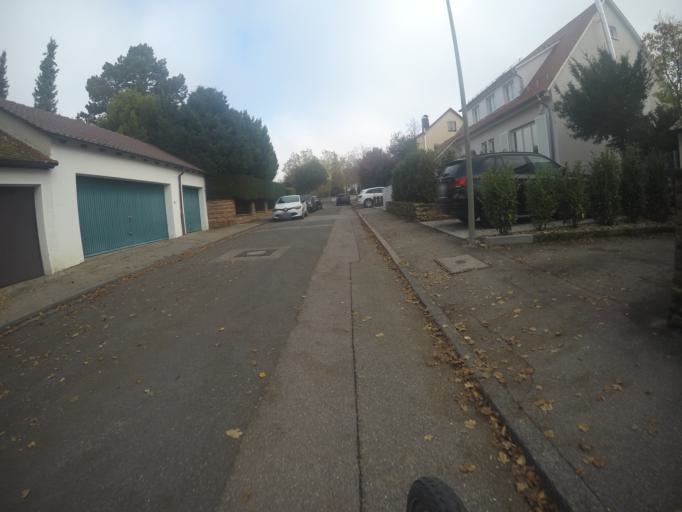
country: DE
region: Baden-Wuerttemberg
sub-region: Regierungsbezirk Stuttgart
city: Stuttgart
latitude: 48.7448
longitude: 9.1582
